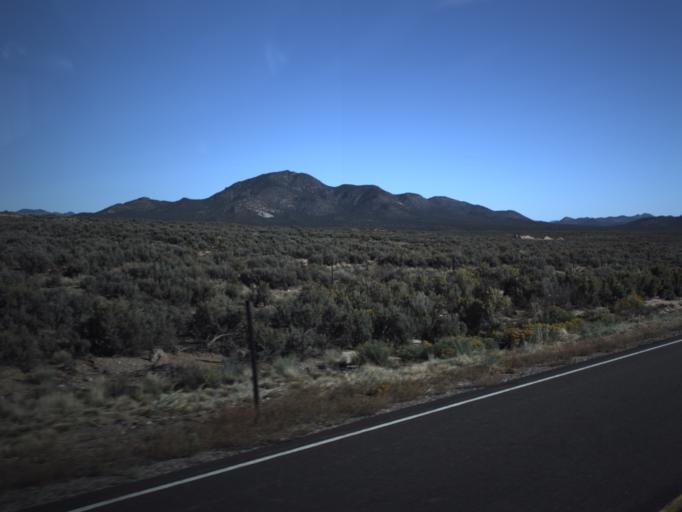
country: US
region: Utah
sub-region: Washington County
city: Enterprise
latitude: 37.7598
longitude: -113.9891
